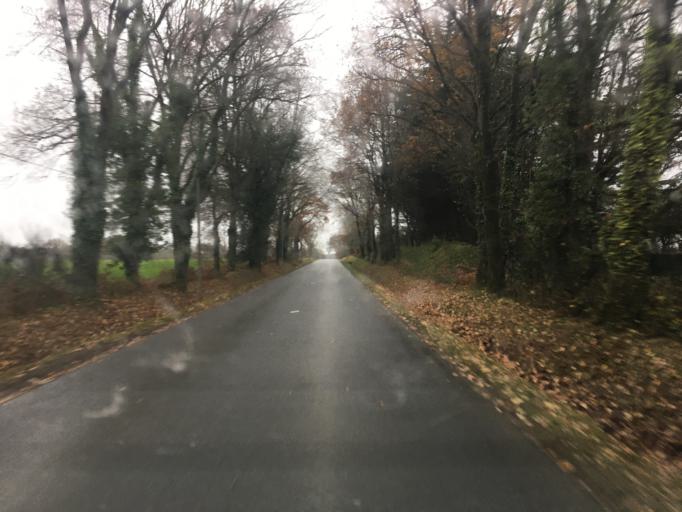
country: FR
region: Brittany
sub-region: Departement du Morbihan
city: Sarzeau
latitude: 47.5344
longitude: -2.6963
